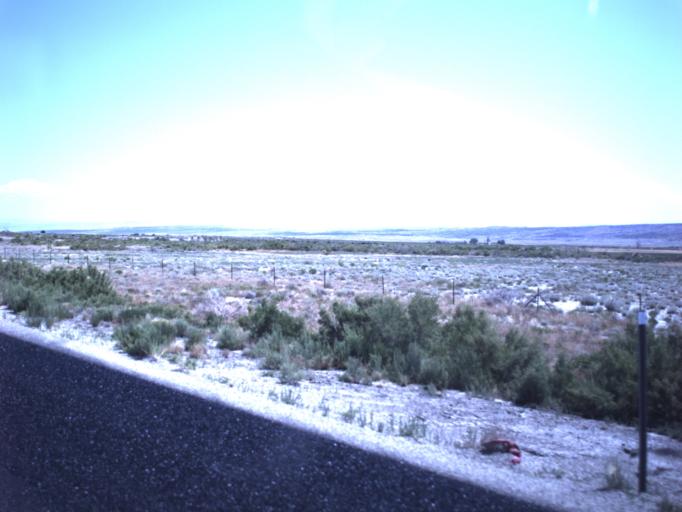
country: US
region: Utah
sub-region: Emery County
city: Ferron
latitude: 38.9963
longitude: -111.1645
